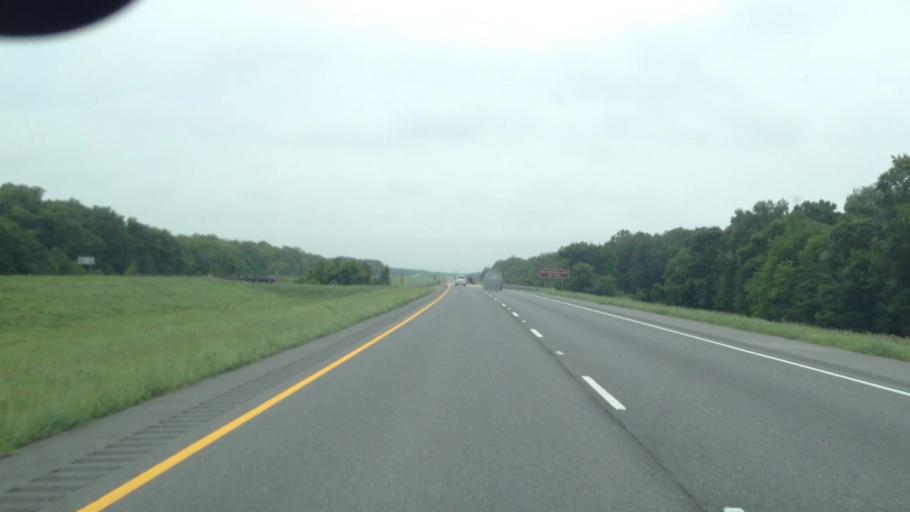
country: US
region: Louisiana
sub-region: Evangeline Parish
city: Ville Platte
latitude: 30.7162
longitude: -92.1054
